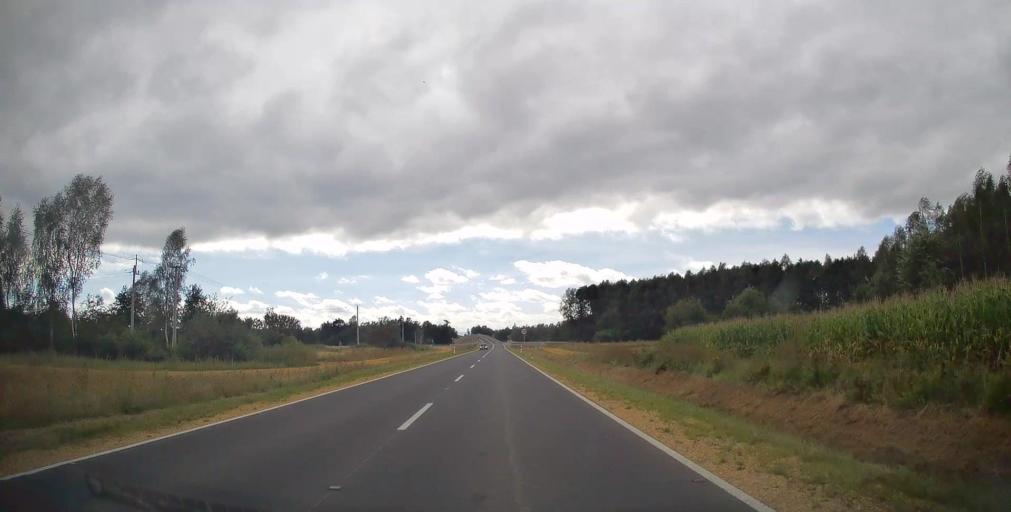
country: PL
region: Lesser Poland Voivodeship
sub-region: Powiat oswiecimski
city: Zator
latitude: 50.0080
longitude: 19.4243
